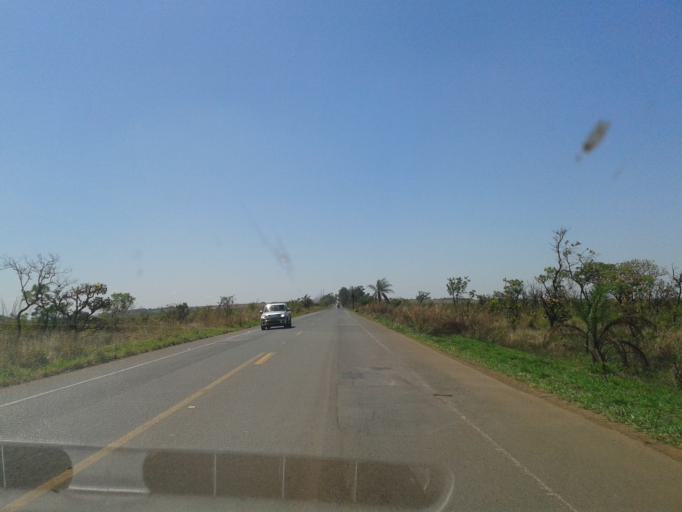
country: BR
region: Minas Gerais
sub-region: Araxa
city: Araxa
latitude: -19.4188
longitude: -47.2837
